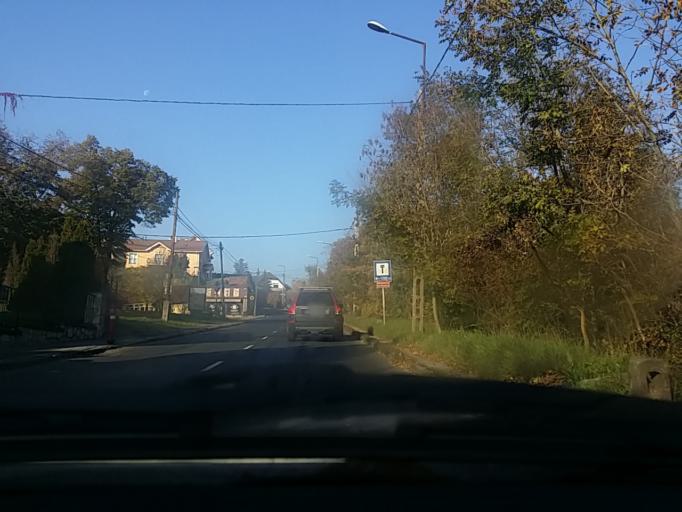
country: HU
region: Budapest
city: Budapest II. keruelet
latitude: 47.5311
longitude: 19.0257
